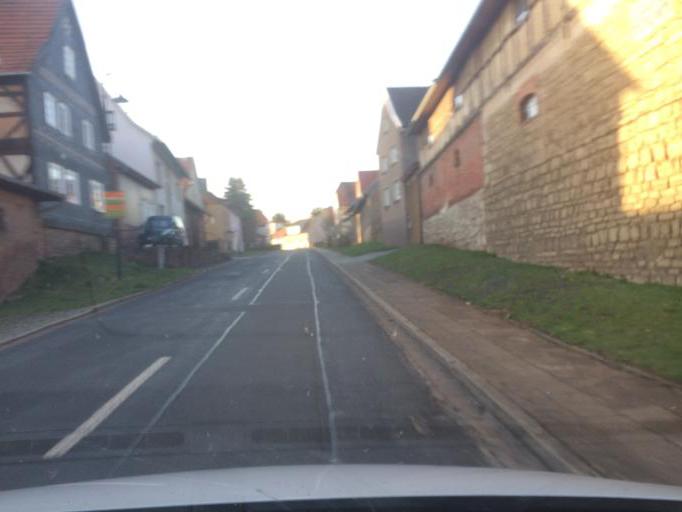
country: DE
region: Thuringia
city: Grossbodungen
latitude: 51.5325
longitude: 10.5034
